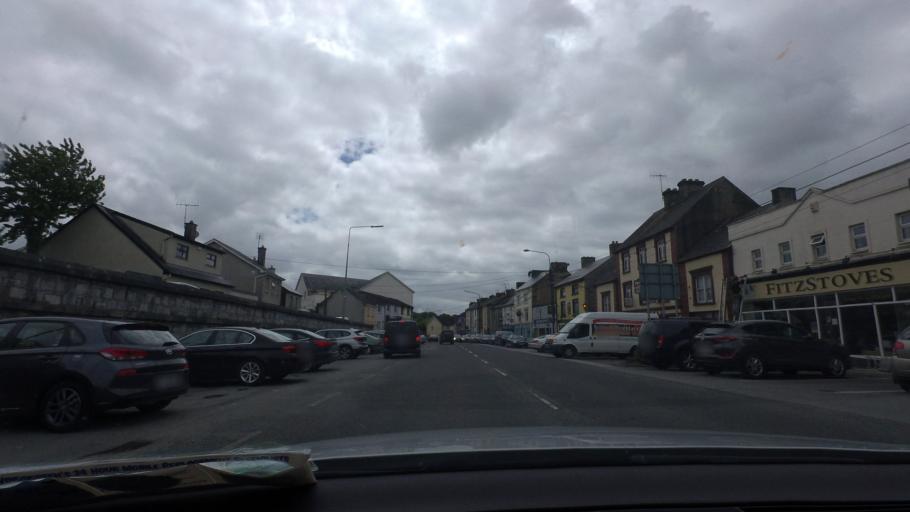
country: IE
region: Munster
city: Cashel
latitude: 52.5193
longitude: -7.8864
